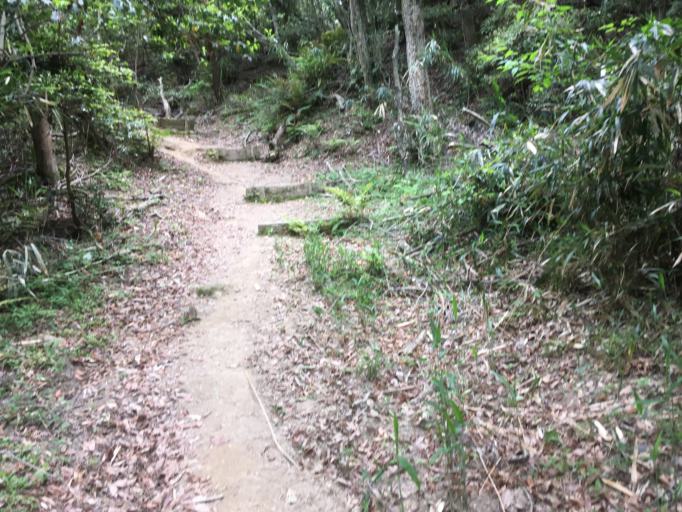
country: JP
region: Nara
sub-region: Ikoma-shi
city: Ikoma
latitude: 34.7008
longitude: 135.6728
